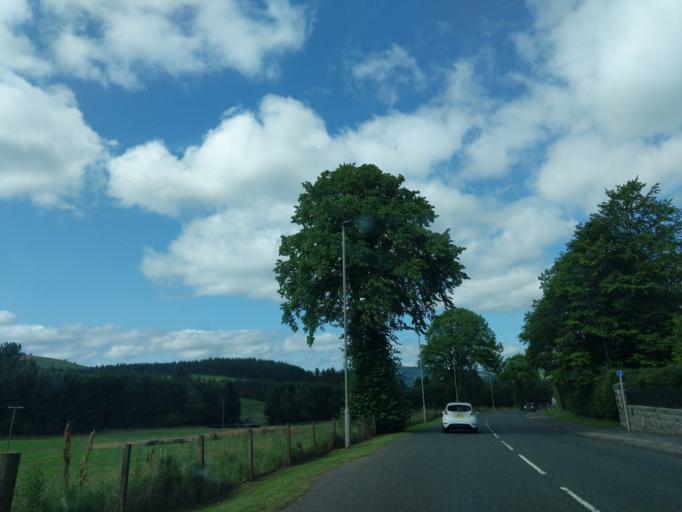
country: GB
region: Scotland
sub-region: Moray
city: Dufftown
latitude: 57.4501
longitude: -3.1310
